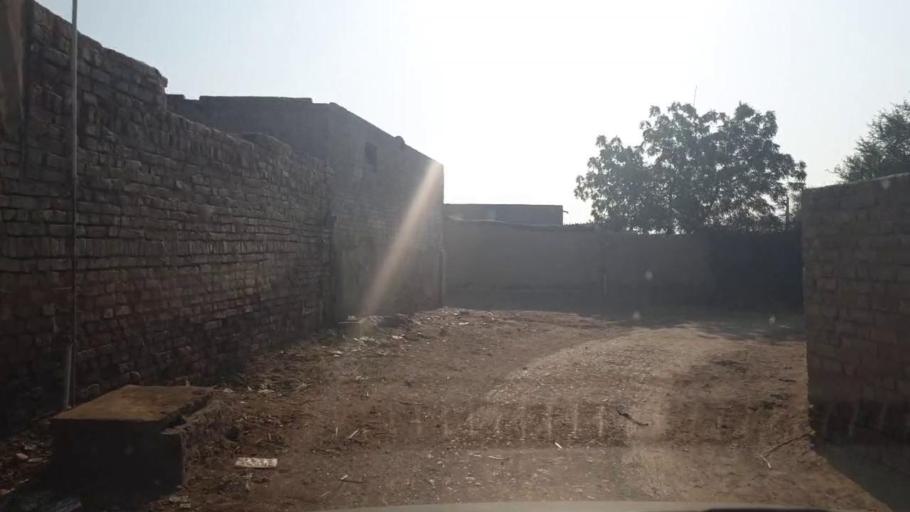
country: PK
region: Sindh
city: Tando Adam
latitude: 25.7481
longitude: 68.6049
